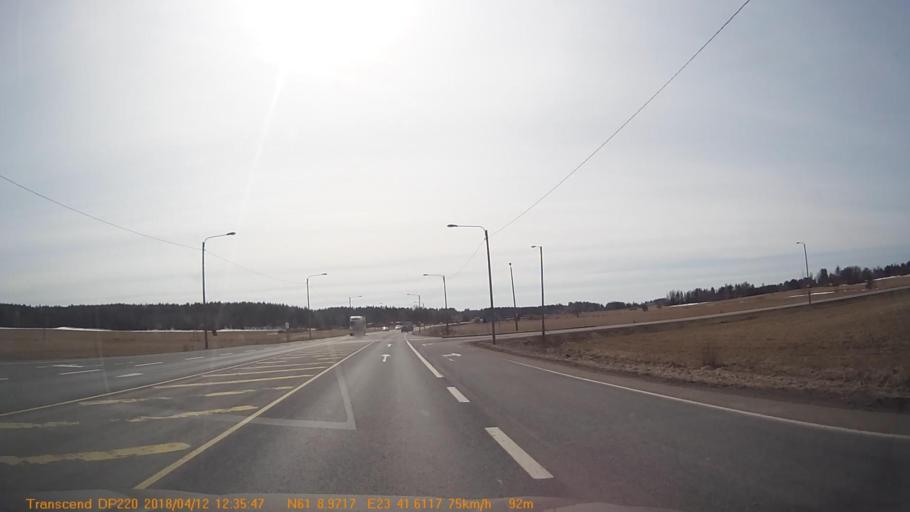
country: FI
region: Pirkanmaa
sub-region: Etelae-Pirkanmaa
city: Kylmaekoski
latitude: 61.1496
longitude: 23.6935
